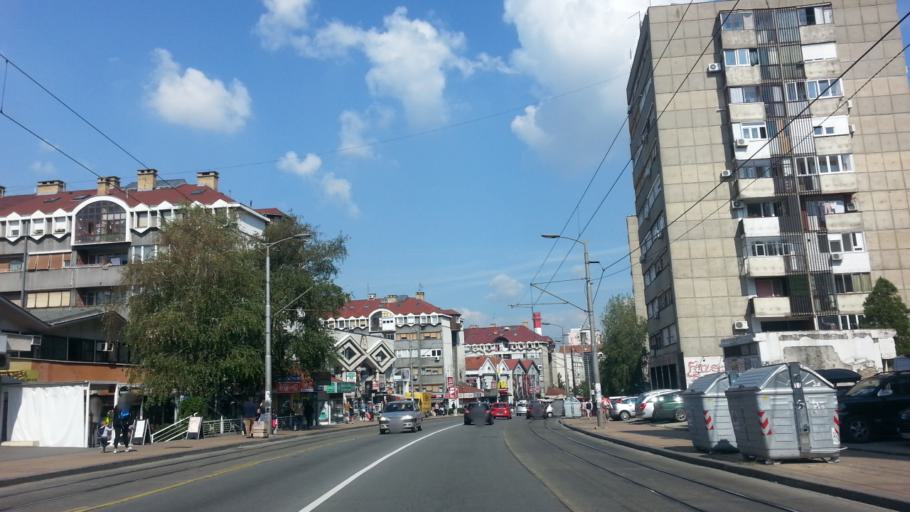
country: RS
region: Central Serbia
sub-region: Belgrade
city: Cukarica
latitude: 44.7762
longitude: 20.4138
